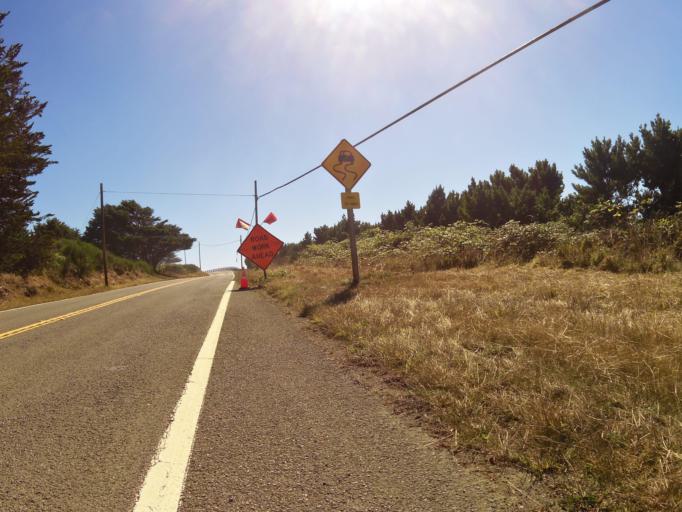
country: US
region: California
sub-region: Mendocino County
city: Fort Bragg
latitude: 39.6549
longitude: -123.7845
